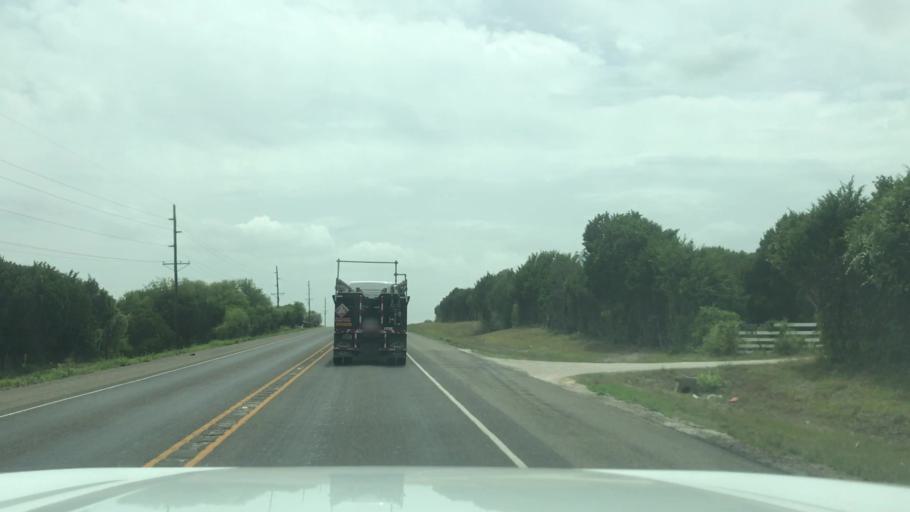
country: US
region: Texas
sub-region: Bosque County
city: Clifton
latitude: 31.7229
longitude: -97.5486
